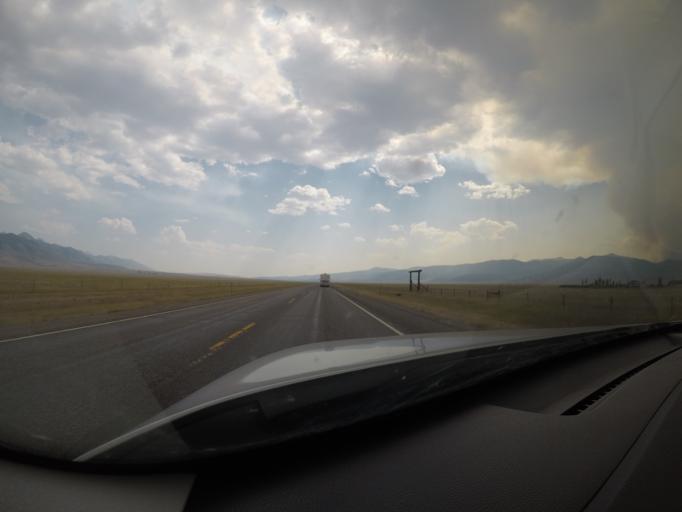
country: US
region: Montana
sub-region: Gallatin County
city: Big Sky
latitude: 45.0616
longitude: -111.6466
